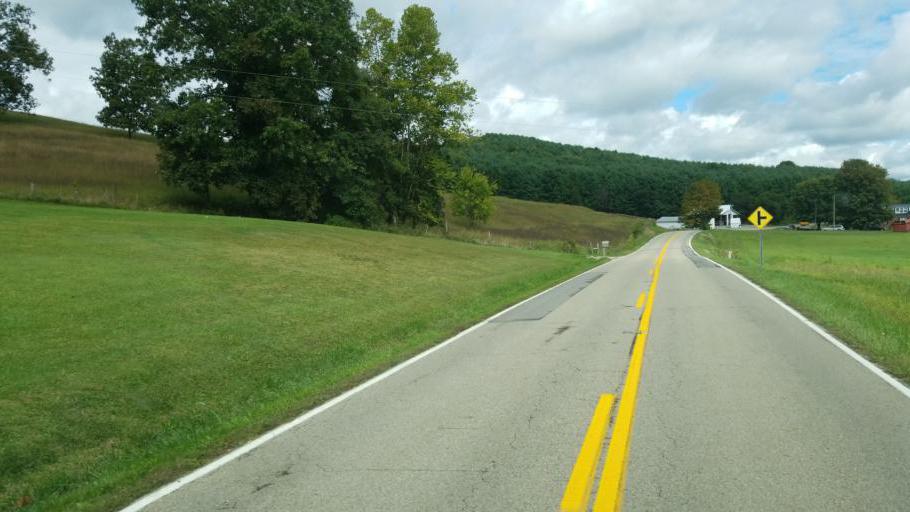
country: US
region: Ohio
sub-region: Jackson County
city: Oak Hill
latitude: 38.8769
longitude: -82.7048
